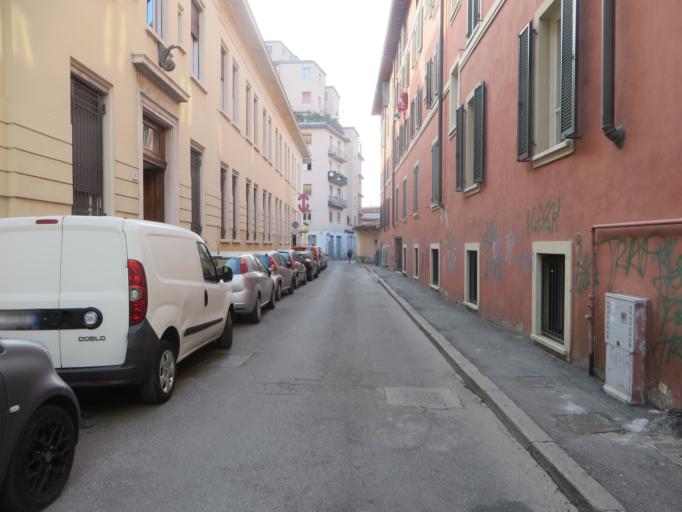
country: IT
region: Lombardy
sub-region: Provincia di Brescia
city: Brescia
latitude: 45.5338
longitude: 10.2115
